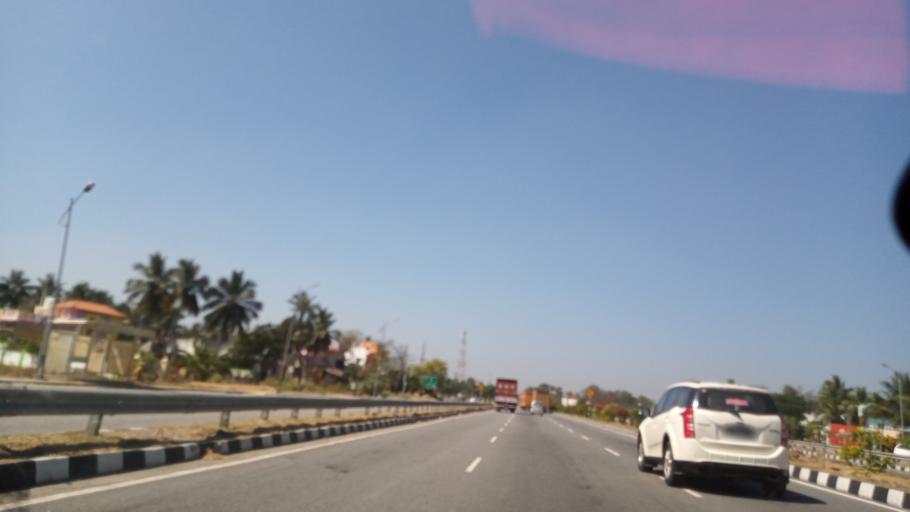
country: IN
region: Tamil Nadu
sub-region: Vellore
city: Jolarpettai
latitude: 12.5963
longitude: 78.5251
